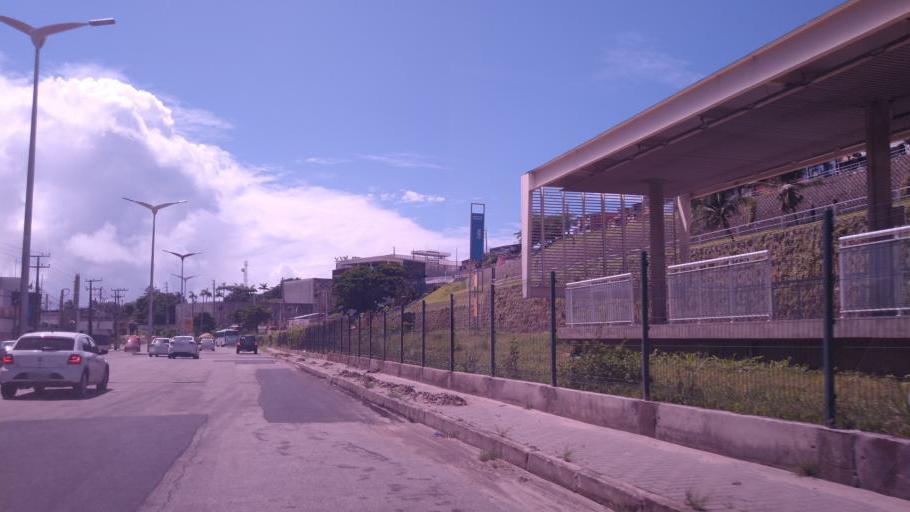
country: BR
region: Ceara
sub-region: Fortaleza
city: Fortaleza
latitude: -3.7204
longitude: -38.4768
